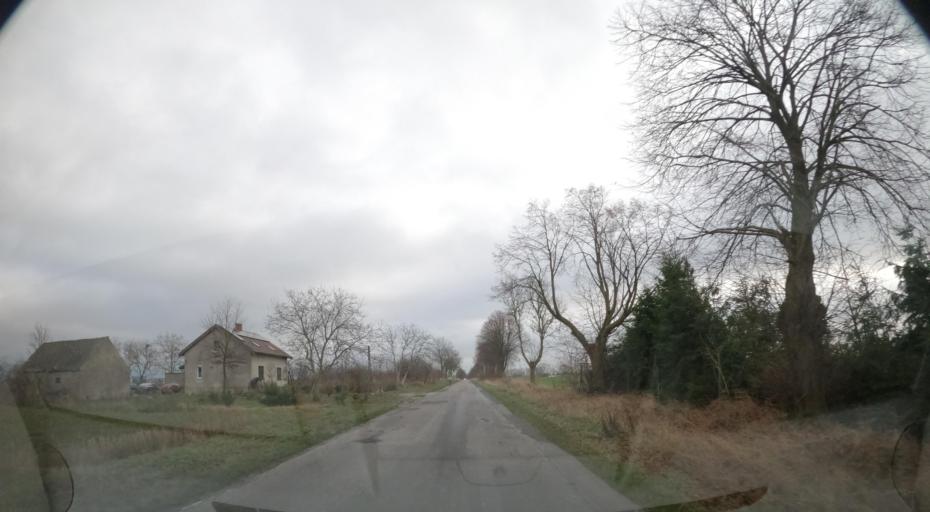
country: PL
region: Greater Poland Voivodeship
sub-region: Powiat pilski
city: Lobzenica
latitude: 53.2614
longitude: 17.2322
